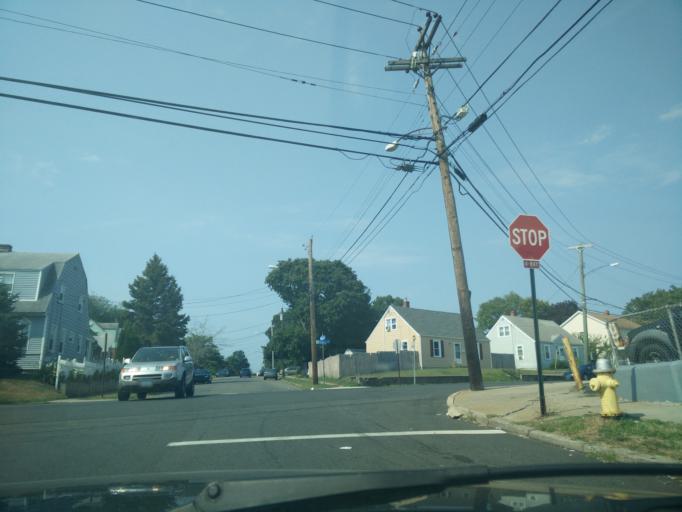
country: US
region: Connecticut
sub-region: Fairfield County
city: Bridgeport
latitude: 41.2055
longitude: -73.2212
